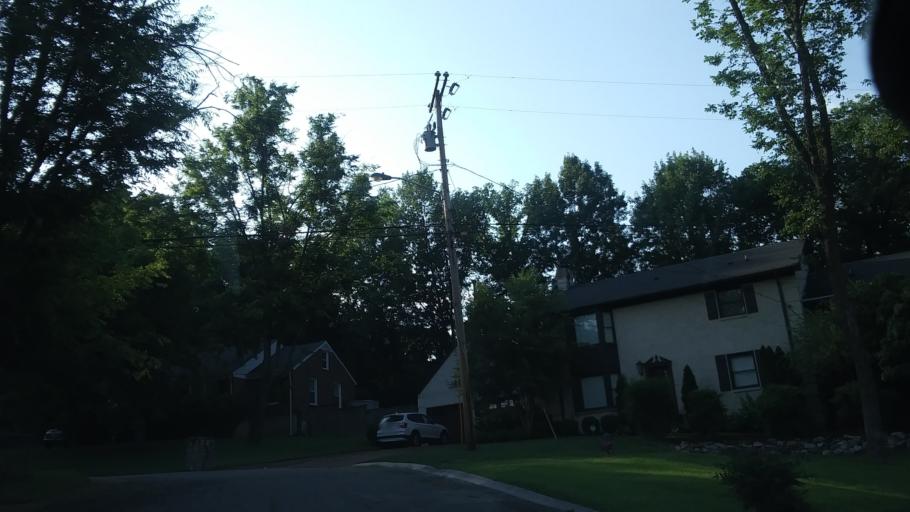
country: US
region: Tennessee
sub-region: Davidson County
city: Belle Meade
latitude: 36.1399
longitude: -86.8603
